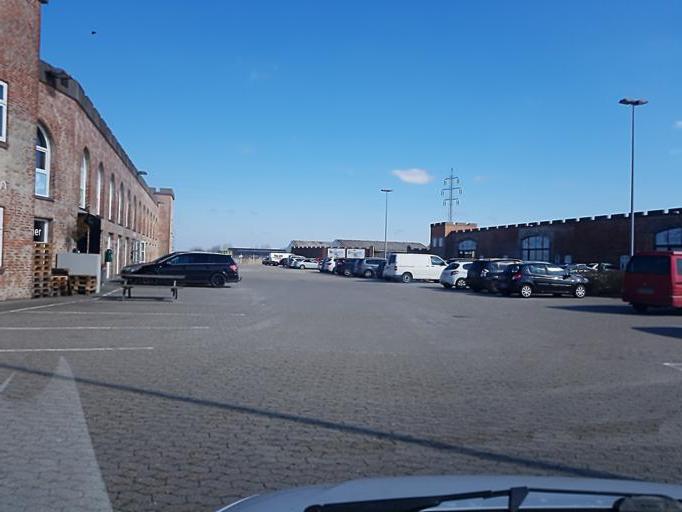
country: DK
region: South Denmark
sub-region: Varde Kommune
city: Varde
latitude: 55.6073
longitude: 8.5060
